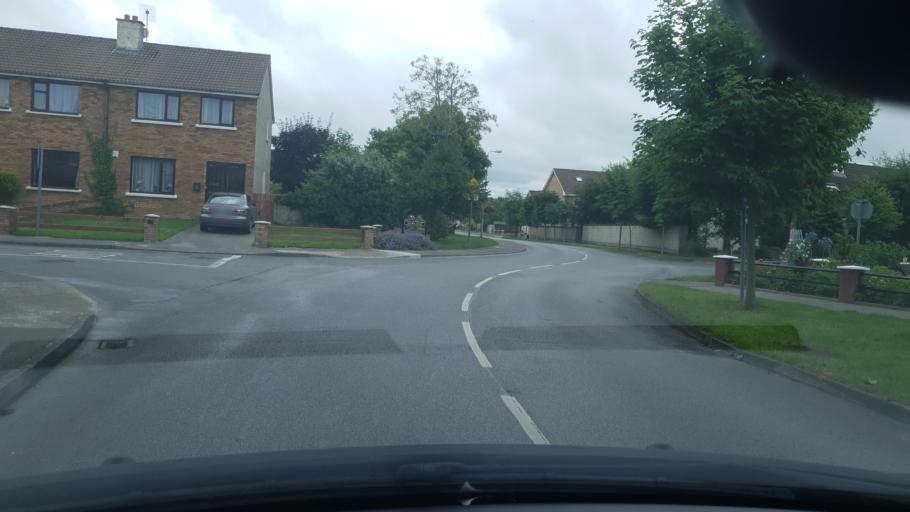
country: IE
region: Munster
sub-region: Ciarrai
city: Tralee
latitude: 52.2593
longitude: -9.6845
